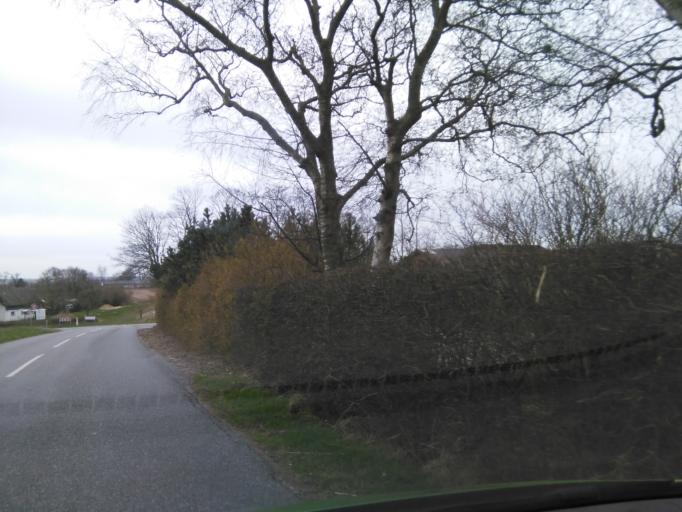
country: DK
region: Central Jutland
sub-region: Arhus Kommune
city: Beder
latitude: 56.0330
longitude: 10.2377
